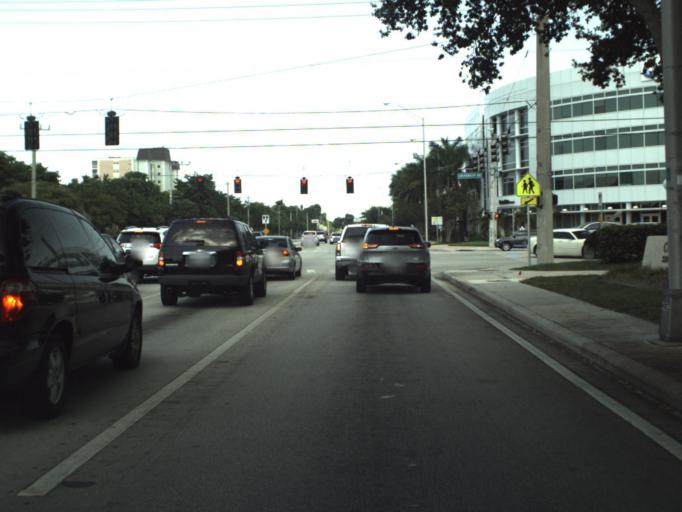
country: US
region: Florida
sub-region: Broward County
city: Coral Springs
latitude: 26.2723
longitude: -80.2508
